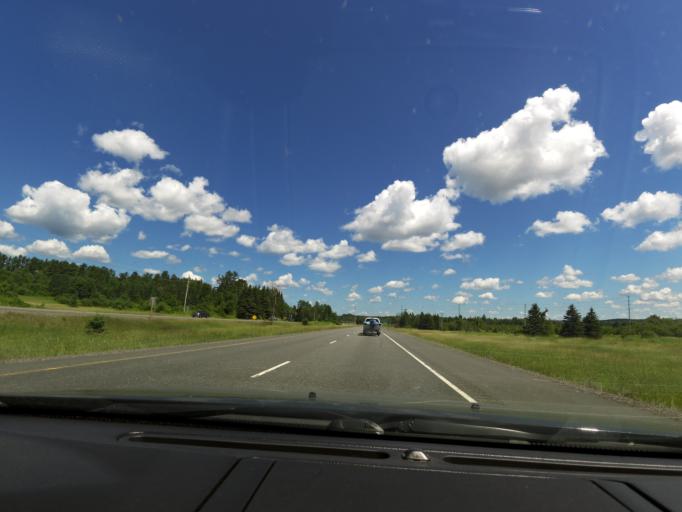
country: CA
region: Ontario
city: Huntsville
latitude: 45.2525
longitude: -79.2969
